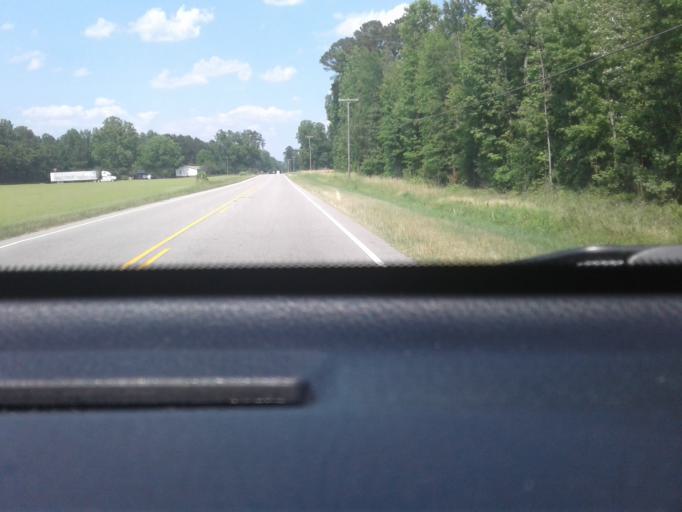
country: US
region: North Carolina
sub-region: Cumberland County
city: Eastover
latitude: 35.1278
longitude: -78.7576
